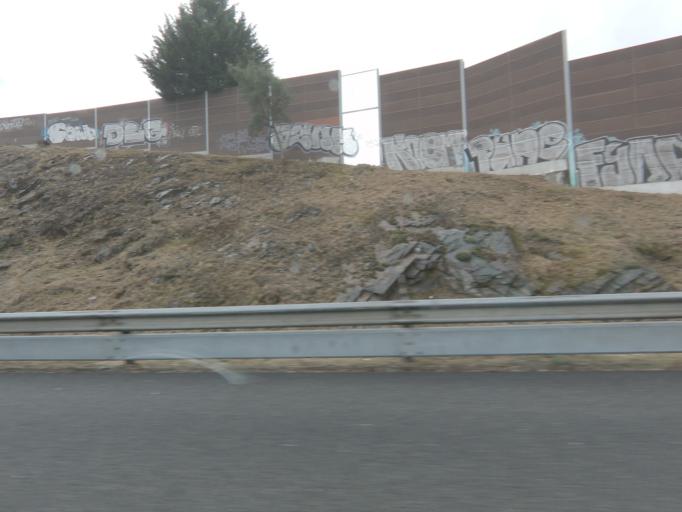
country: PT
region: Porto
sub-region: Valongo
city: Valongo
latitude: 41.1973
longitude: -8.5095
